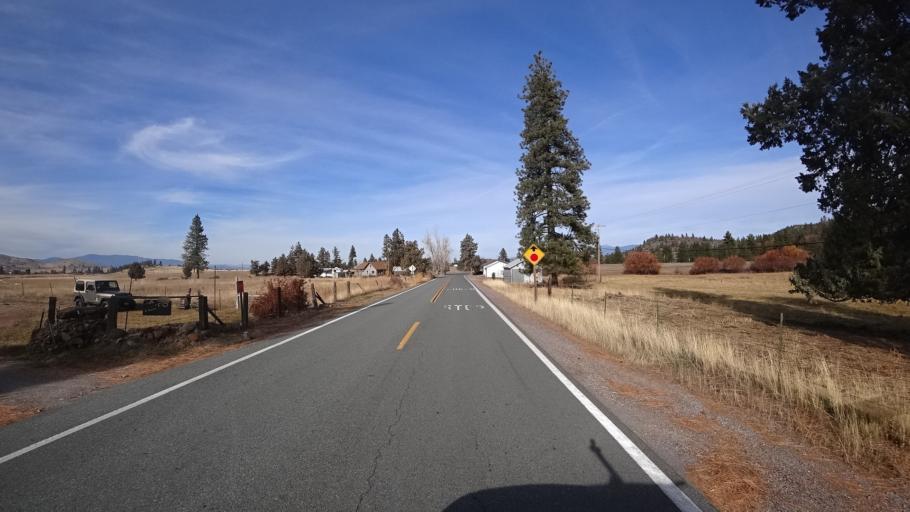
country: US
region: California
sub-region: Siskiyou County
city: Weed
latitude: 41.4387
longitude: -122.4355
